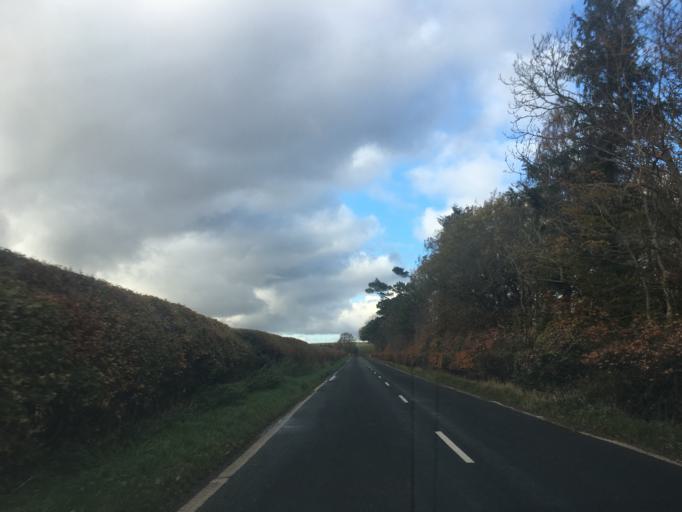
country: GB
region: Scotland
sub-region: East Lothian
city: Pencaitland
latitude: 55.8458
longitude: -2.8727
